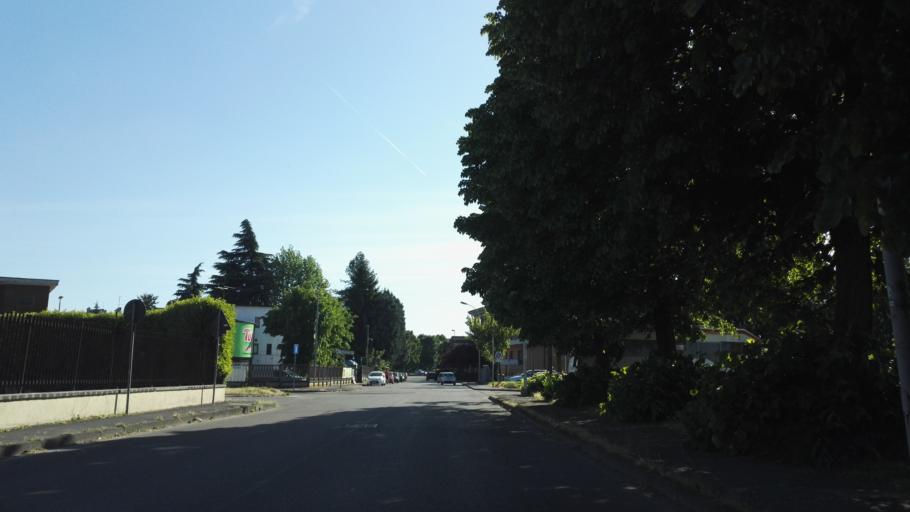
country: IT
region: Lombardy
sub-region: Citta metropolitana di Milano
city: San Giuliano Milanese
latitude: 45.3977
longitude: 9.2915
